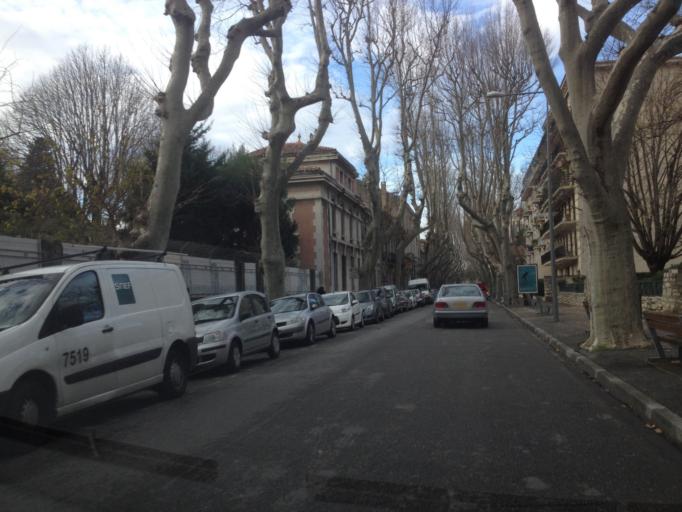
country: FR
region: Provence-Alpes-Cote d'Azur
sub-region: Departement du Vaucluse
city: Avignon
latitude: 43.9446
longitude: 4.8027
